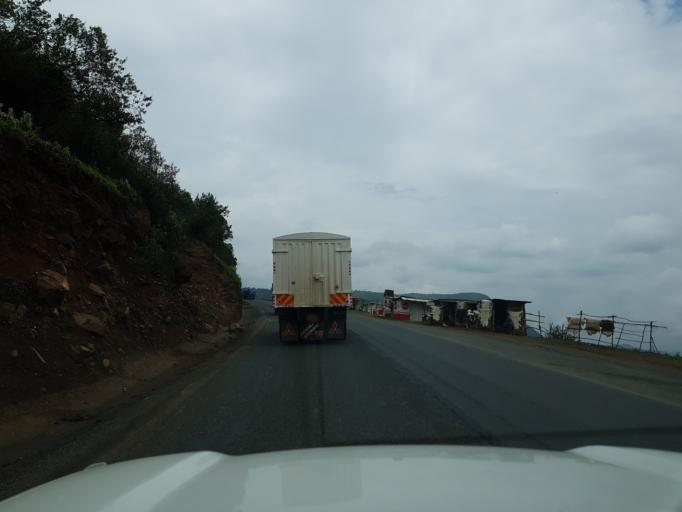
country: KE
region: Kiambu
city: Limuru
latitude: -1.0514
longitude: 36.6017
